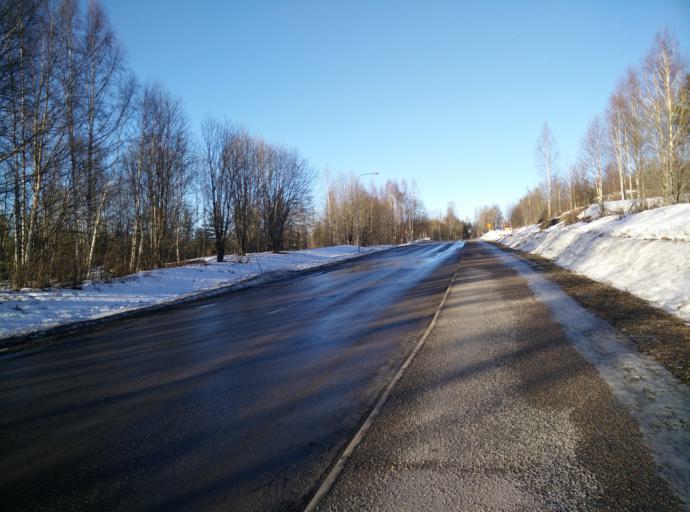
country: SE
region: Vaesternorrland
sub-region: Sundsvalls Kommun
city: Skottsund
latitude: 62.3133
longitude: 17.3930
